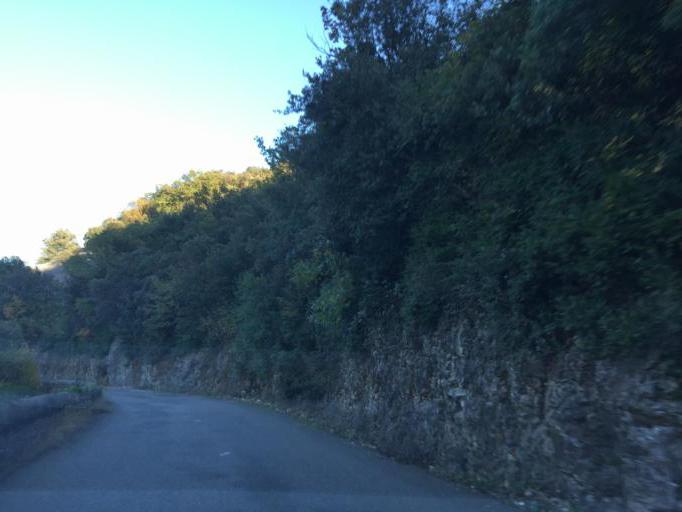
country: FR
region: Rhone-Alpes
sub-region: Departement de l'Ardeche
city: Bourg-Saint-Andeol
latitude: 44.4455
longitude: 4.6027
